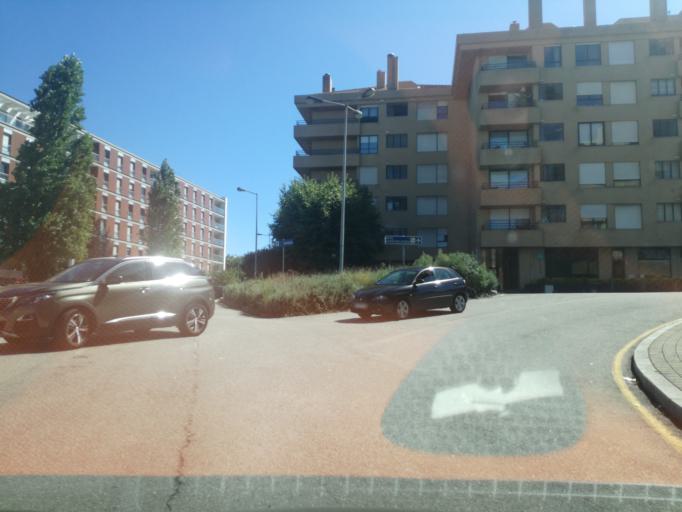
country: PT
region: Porto
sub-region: Matosinhos
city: Sao Mamede de Infesta
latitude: 41.1846
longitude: -8.6011
